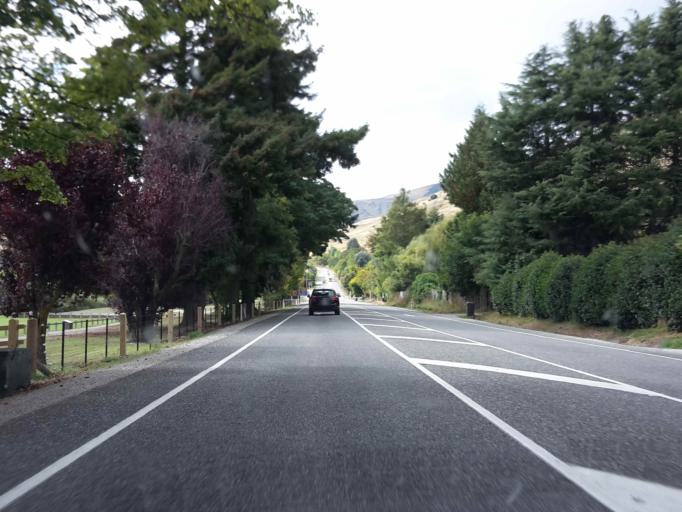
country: NZ
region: Otago
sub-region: Queenstown-Lakes District
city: Arrowtown
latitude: -44.9900
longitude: 168.8104
